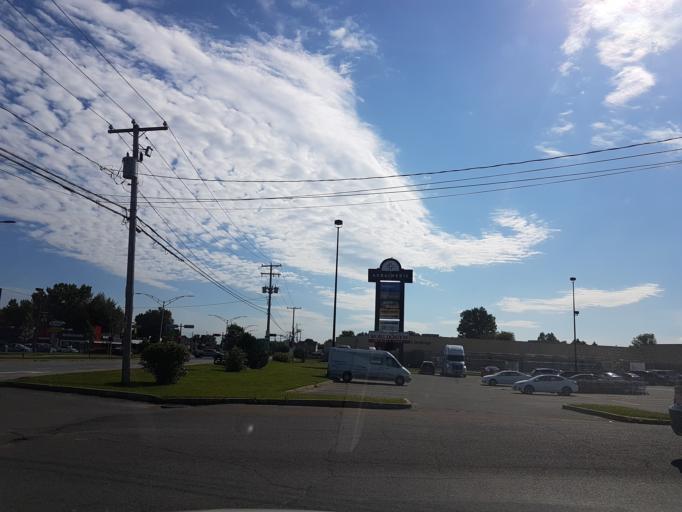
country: CA
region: Quebec
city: Sainte-Catherine
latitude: 46.3252
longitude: -72.5640
